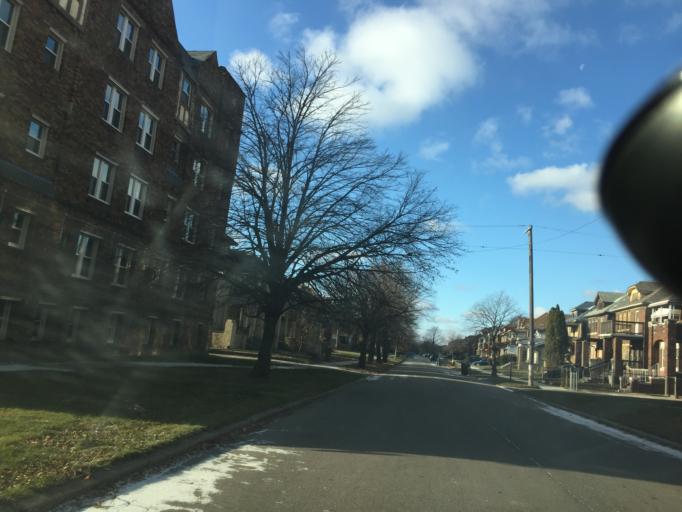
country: US
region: Michigan
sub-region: Wayne County
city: Highland Park
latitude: 42.3913
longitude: -83.1338
